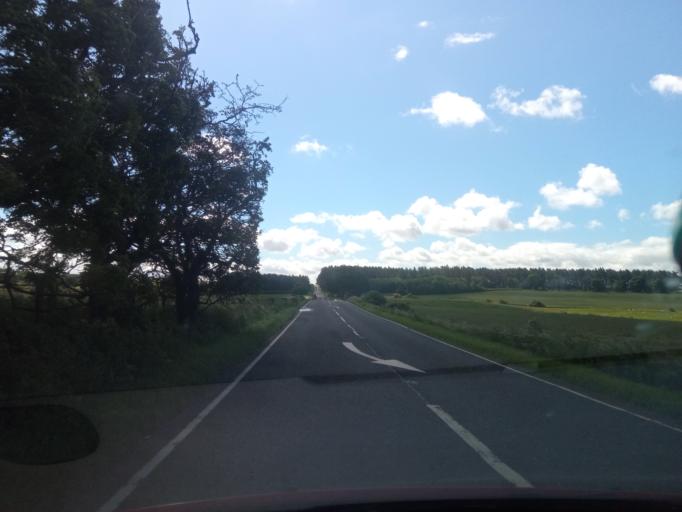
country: GB
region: England
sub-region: Northumberland
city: Acomb
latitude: 55.0683
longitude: -2.0823
